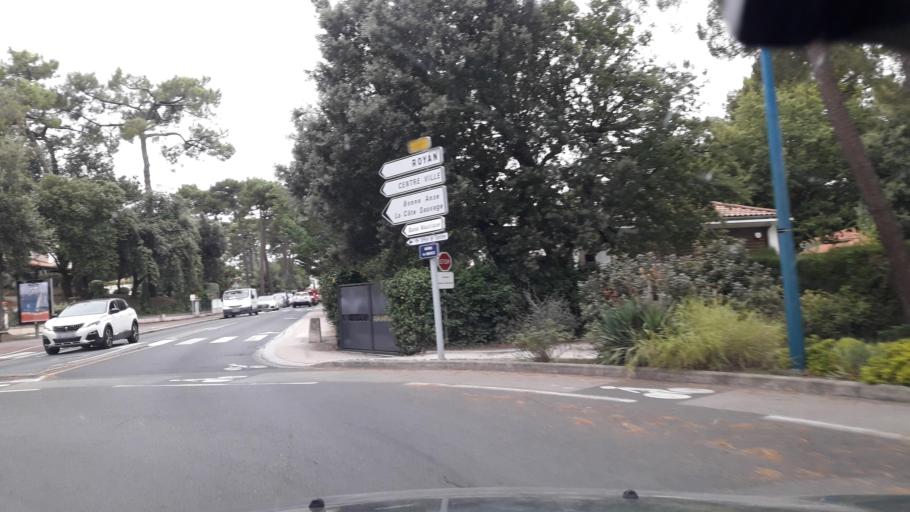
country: FR
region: Poitou-Charentes
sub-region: Departement de la Charente-Maritime
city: Les Mathes
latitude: 45.6942
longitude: -1.1776
